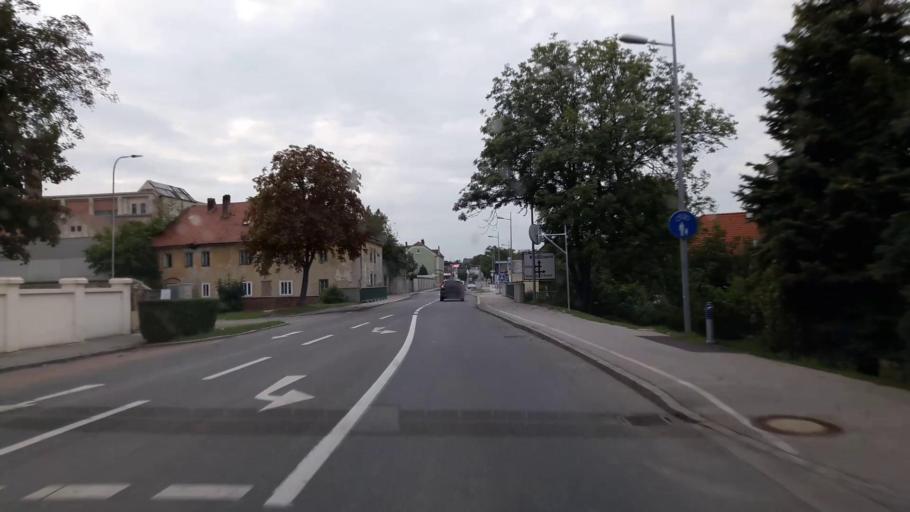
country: AT
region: Lower Austria
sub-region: Politischer Bezirk Wien-Umgebung
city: Schwadorf
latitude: 48.0699
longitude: 16.5854
